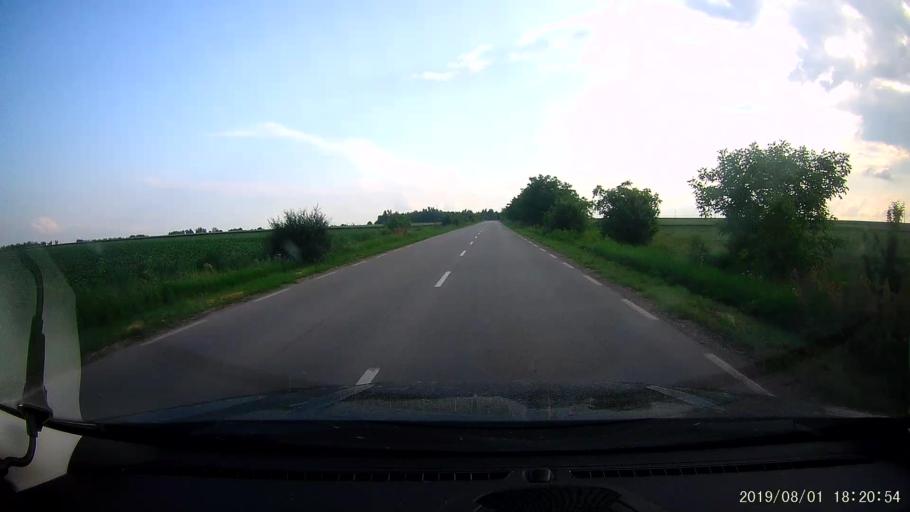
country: BG
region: Shumen
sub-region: Obshtina Kaolinovo
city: Kaolinovo
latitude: 43.6618
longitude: 27.0813
